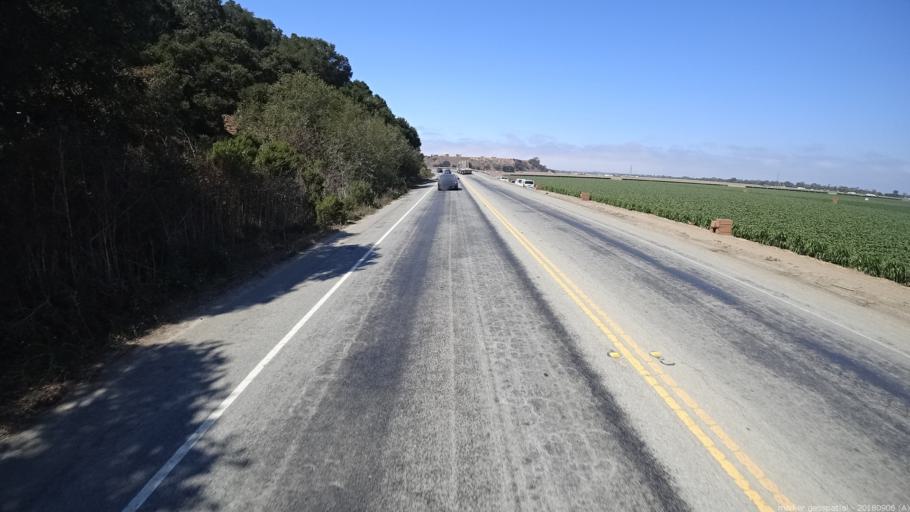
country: US
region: California
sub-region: Monterey County
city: Boronda
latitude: 36.6458
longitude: -121.7181
